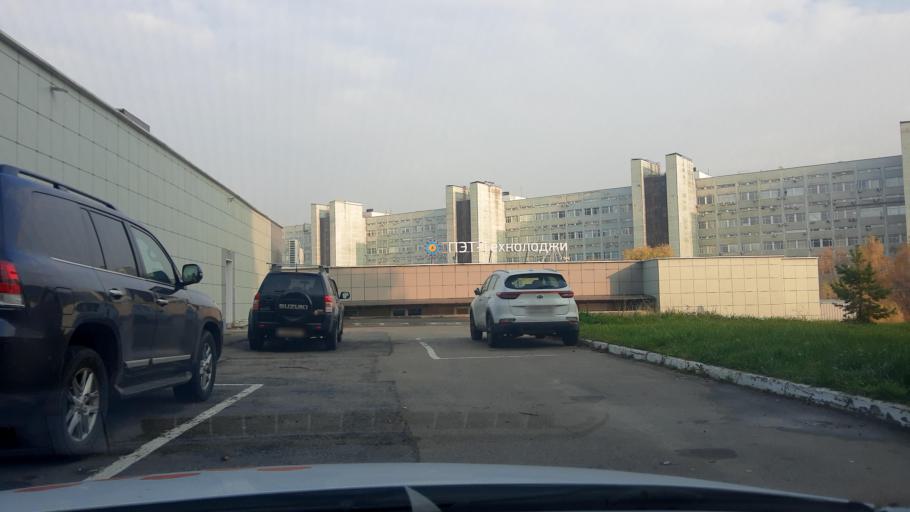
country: RU
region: Moskovskaya
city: Cheremushki
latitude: 55.6530
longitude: 37.5332
